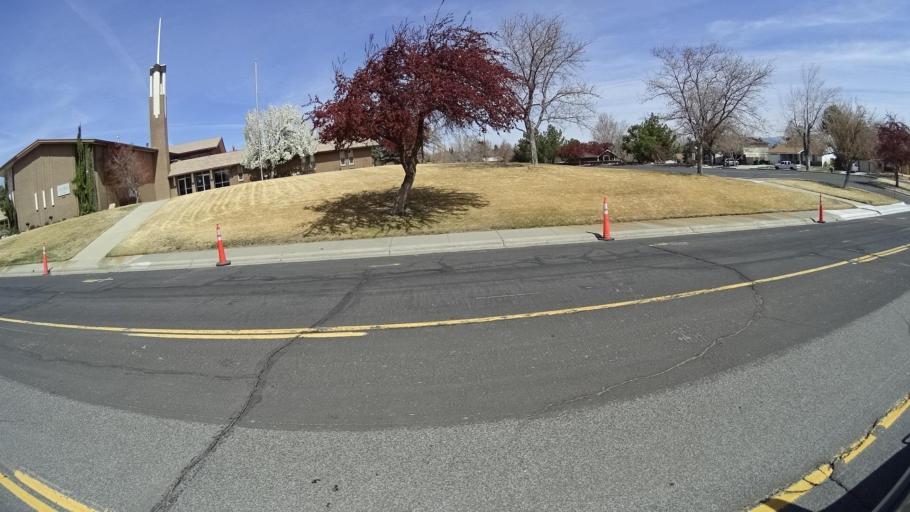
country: US
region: Nevada
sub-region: Washoe County
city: Reno
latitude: 39.5373
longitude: -119.8472
